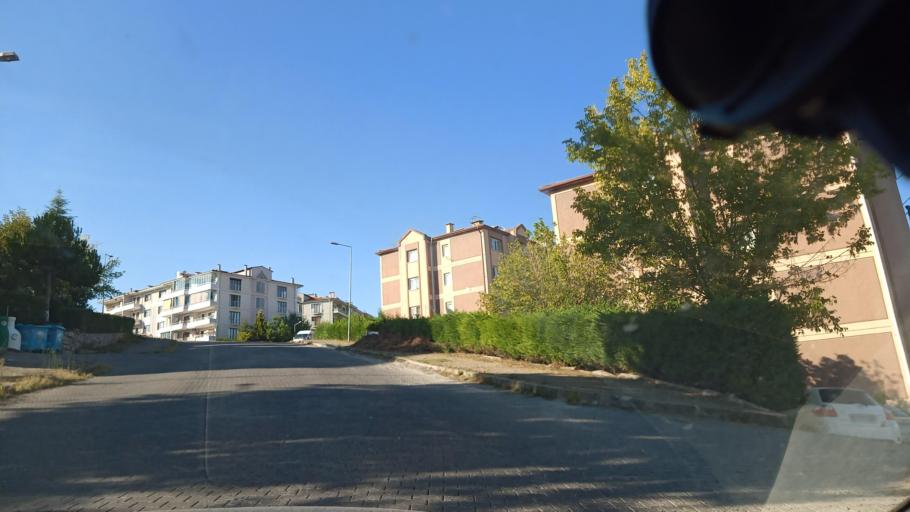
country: TR
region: Sakarya
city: Kazimpasa
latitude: 40.8595
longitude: 30.2923
